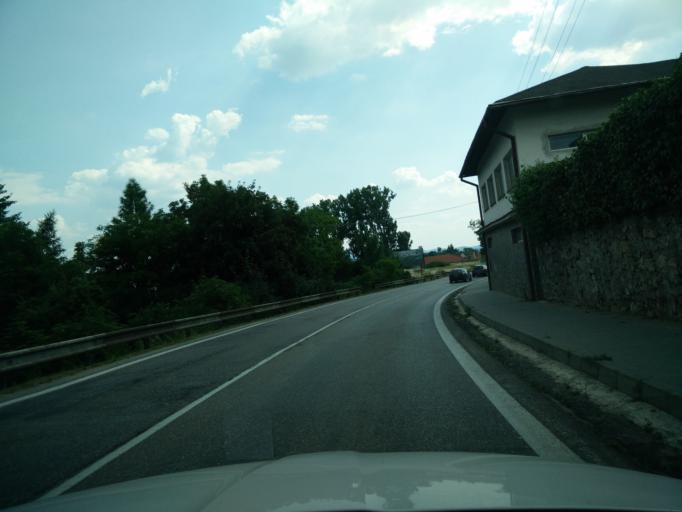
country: SK
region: Nitriansky
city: Partizanske
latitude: 48.6221
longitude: 18.3029
